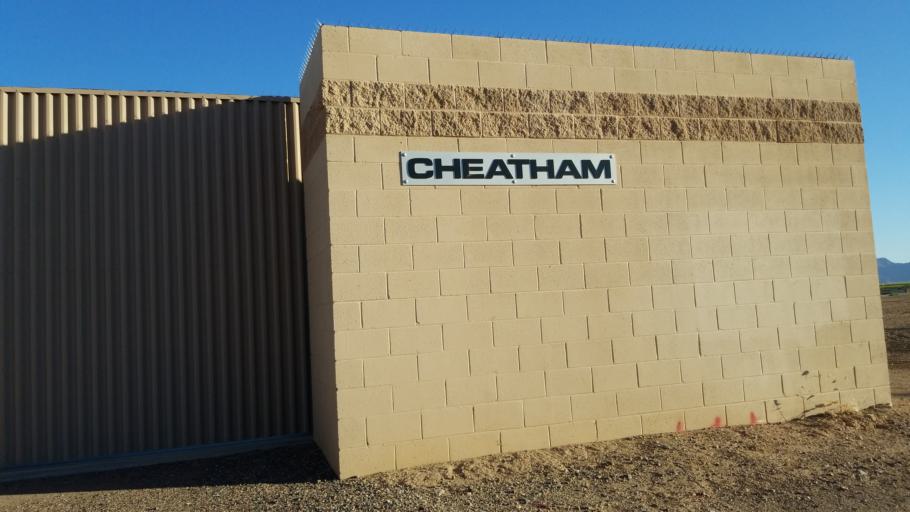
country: US
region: Arizona
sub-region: Maricopa County
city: Laveen
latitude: 33.3772
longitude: -112.1819
